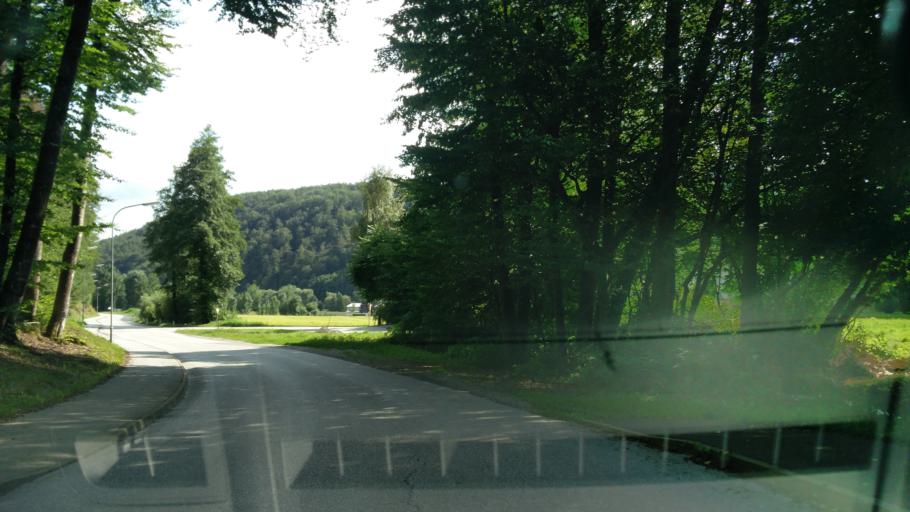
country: AT
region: Styria
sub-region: Politischer Bezirk Weiz
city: Naas
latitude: 47.2369
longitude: 15.6109
